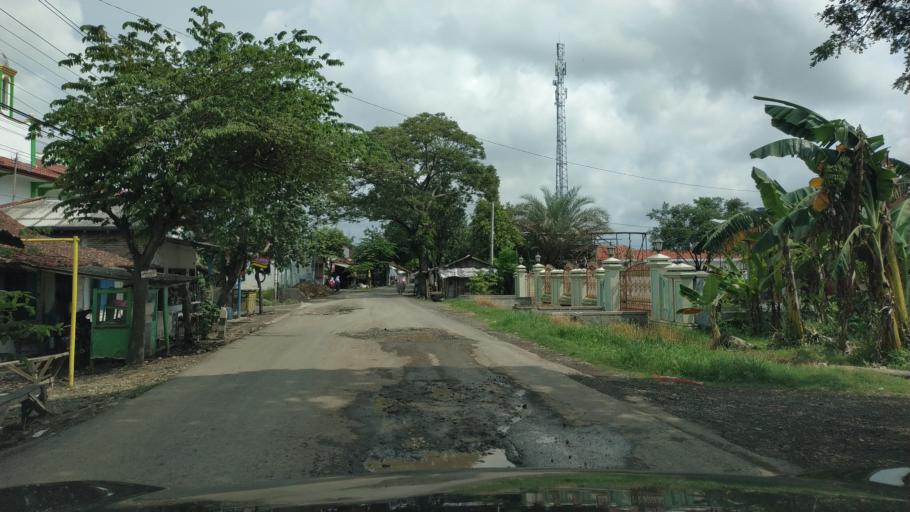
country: ID
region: Central Java
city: Pemalang
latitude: -6.8941
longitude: 109.3271
